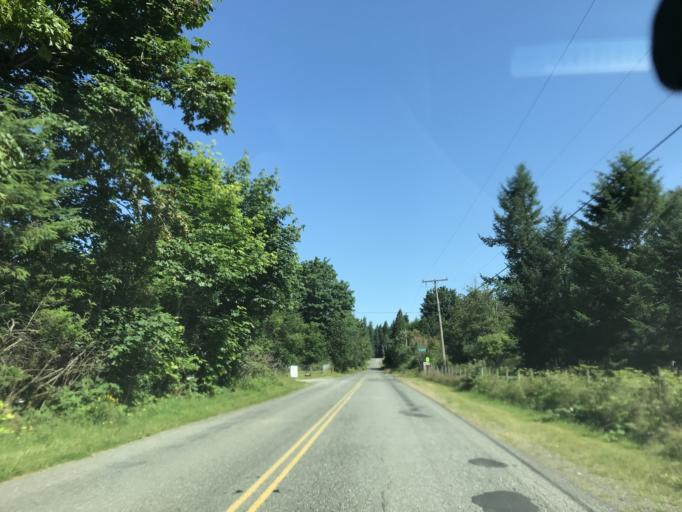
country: US
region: Washington
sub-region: King County
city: Ravensdale
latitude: 47.3654
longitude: -121.8802
